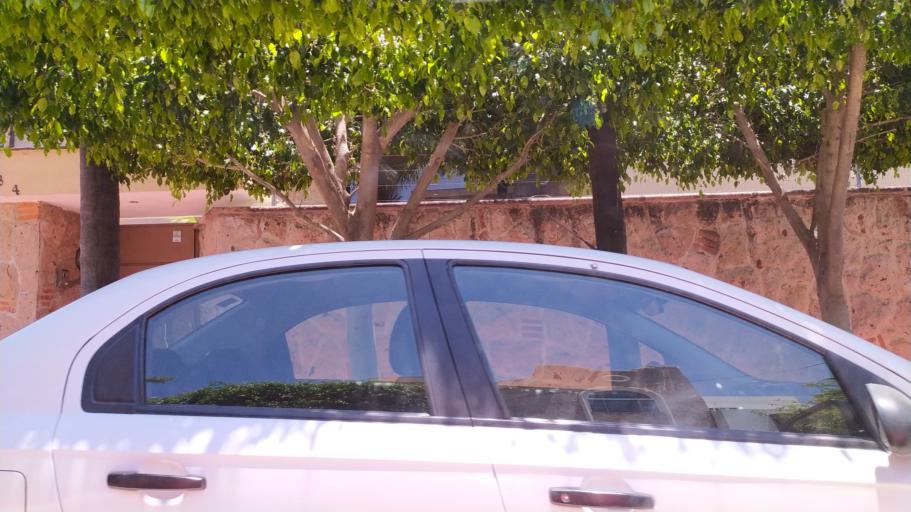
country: MX
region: Jalisco
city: Guadalajara
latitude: 20.6842
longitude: -103.4048
